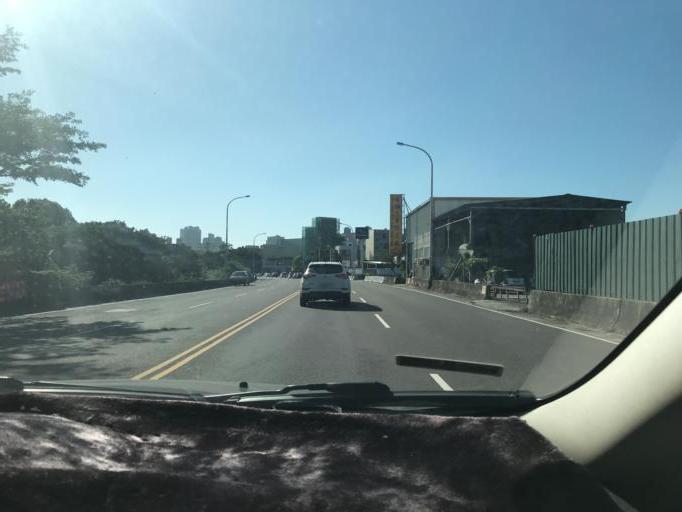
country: TW
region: Taiwan
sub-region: Hsinchu
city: Hsinchu
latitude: 24.8177
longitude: 120.9866
